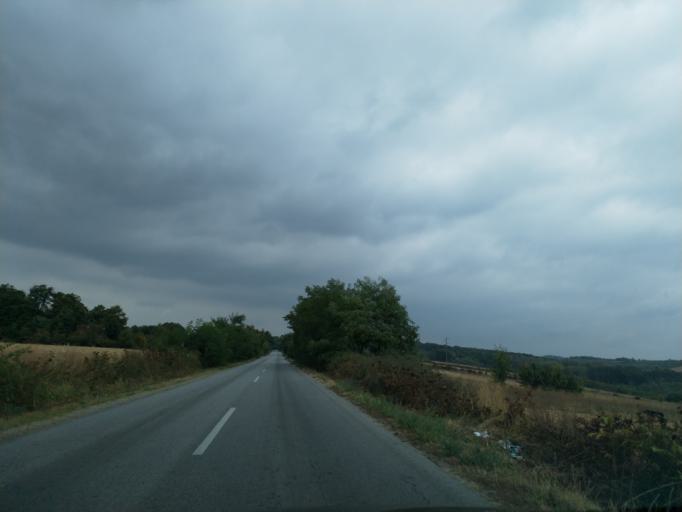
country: RS
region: Central Serbia
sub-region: Pomoravski Okrug
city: Jagodina
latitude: 44.0022
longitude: 21.2116
